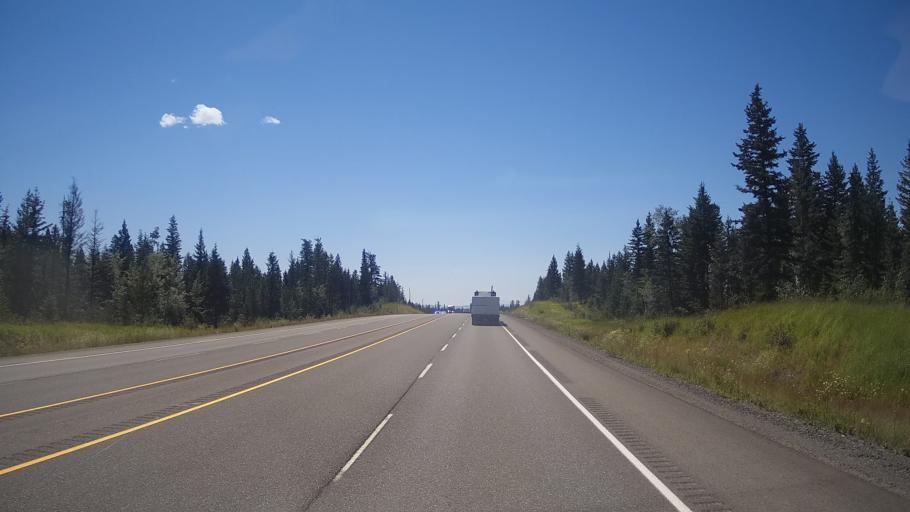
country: CA
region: British Columbia
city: Cache Creek
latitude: 51.4049
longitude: -121.3744
